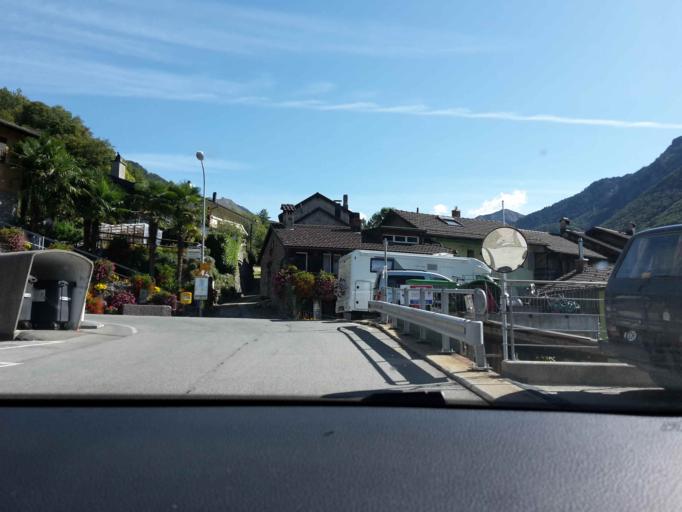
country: CH
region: Ticino
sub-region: Bellinzona District
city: Bellinzona
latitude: 46.1690
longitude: 9.0567
